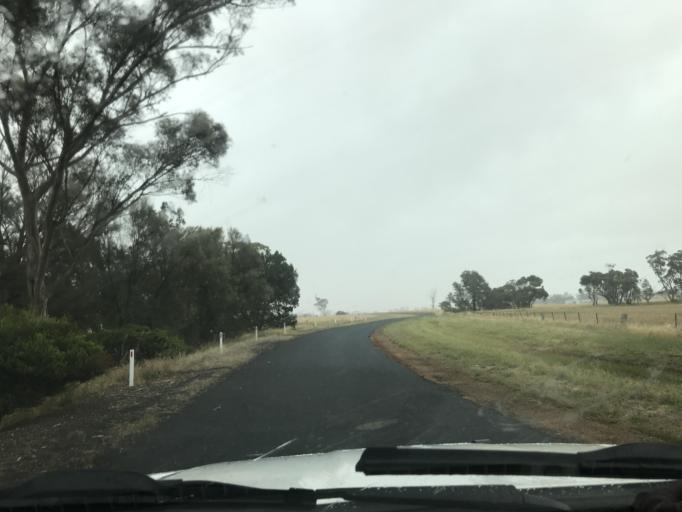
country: AU
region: South Australia
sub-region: Tatiara
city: Bordertown
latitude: -36.3207
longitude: 141.1992
